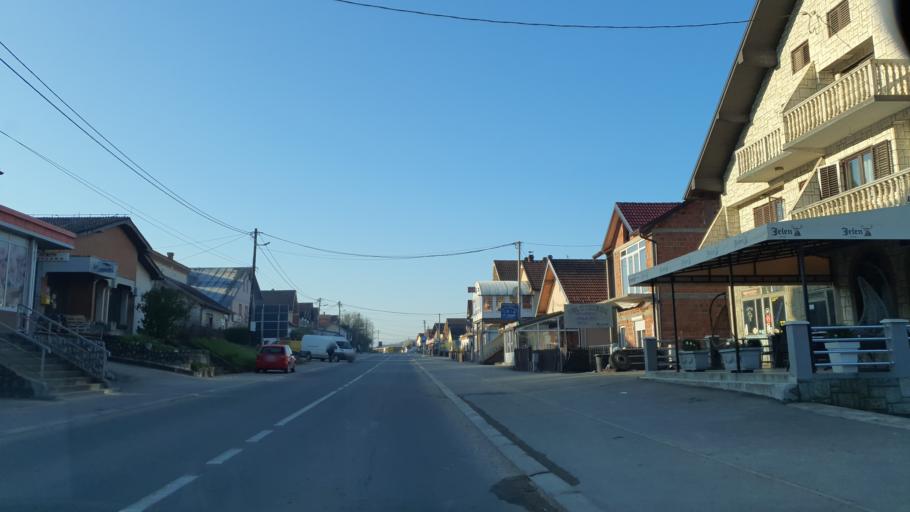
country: RS
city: Bukor
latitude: 44.4552
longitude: 19.4836
